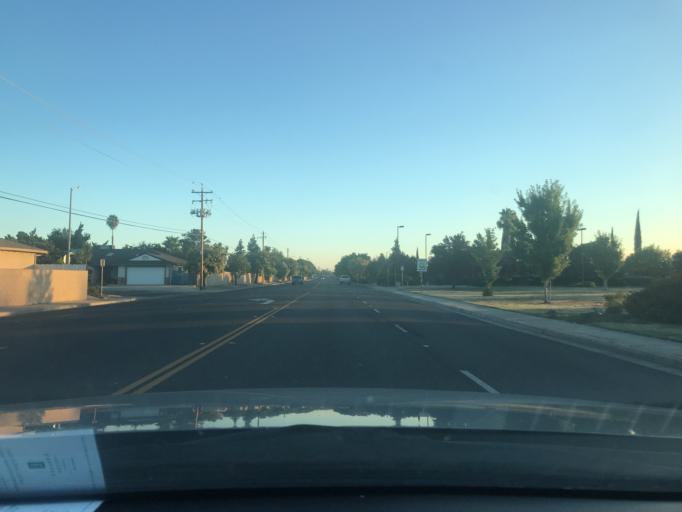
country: US
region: California
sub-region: Merced County
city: Atwater
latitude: 37.3501
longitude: -120.5959
